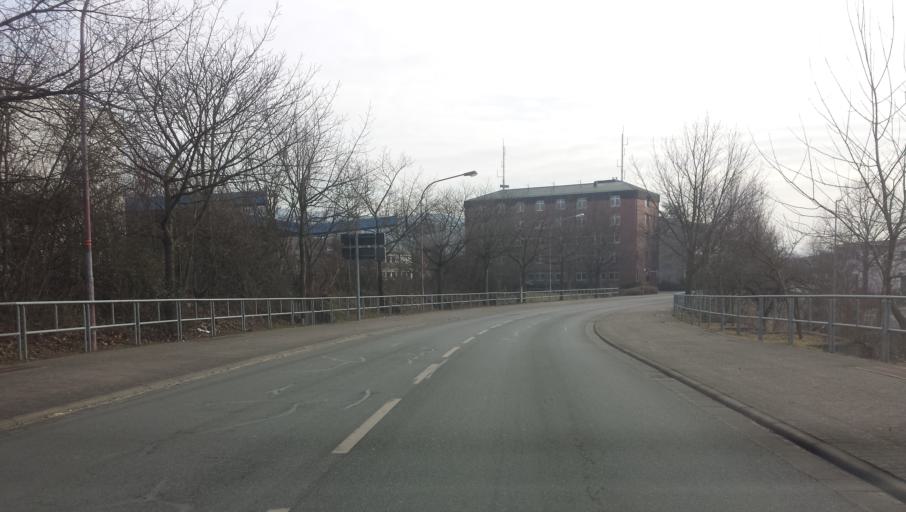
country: DE
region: Hesse
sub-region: Regierungsbezirk Darmstadt
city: Heppenheim an der Bergstrasse
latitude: 49.6485
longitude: 8.6281
